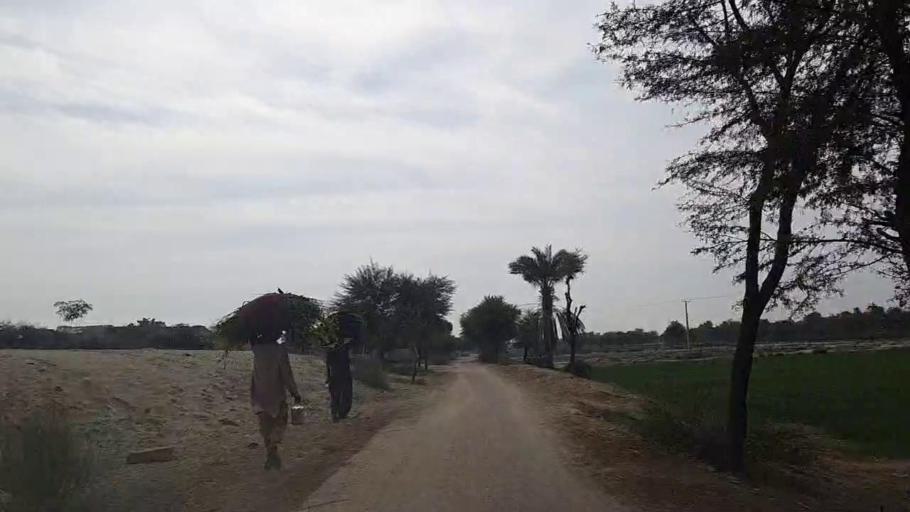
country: PK
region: Sindh
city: Daur
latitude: 26.4329
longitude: 68.4722
